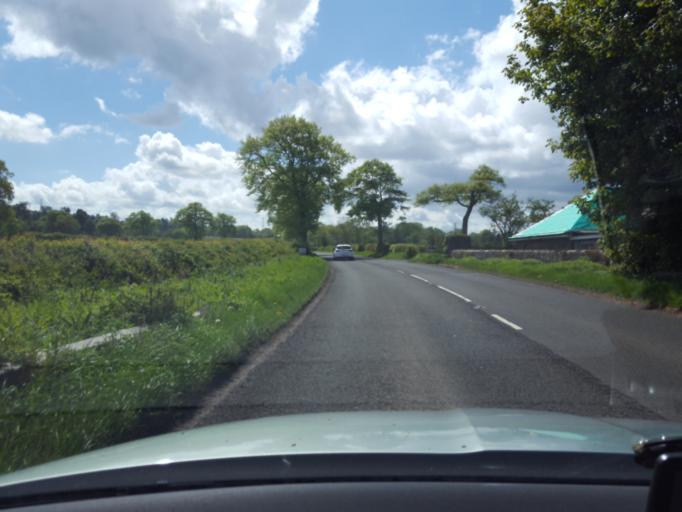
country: GB
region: Scotland
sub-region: Angus
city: Brechin
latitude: 56.7678
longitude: -2.6442
